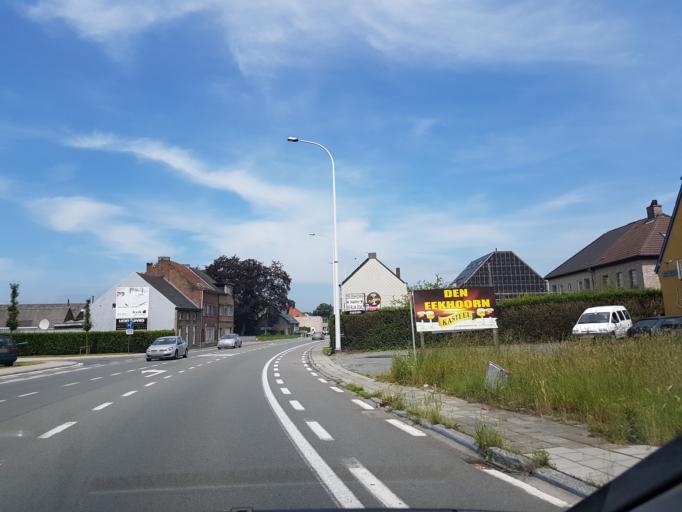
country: BE
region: Flanders
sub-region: Provincie Oost-Vlaanderen
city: Denderleeuw
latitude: 50.9183
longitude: 4.0714
